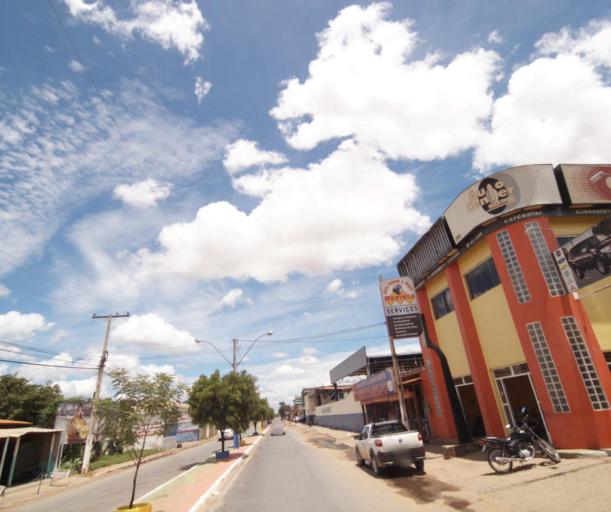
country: BR
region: Bahia
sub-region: Bom Jesus Da Lapa
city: Bom Jesus da Lapa
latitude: -13.2643
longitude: -43.4112
